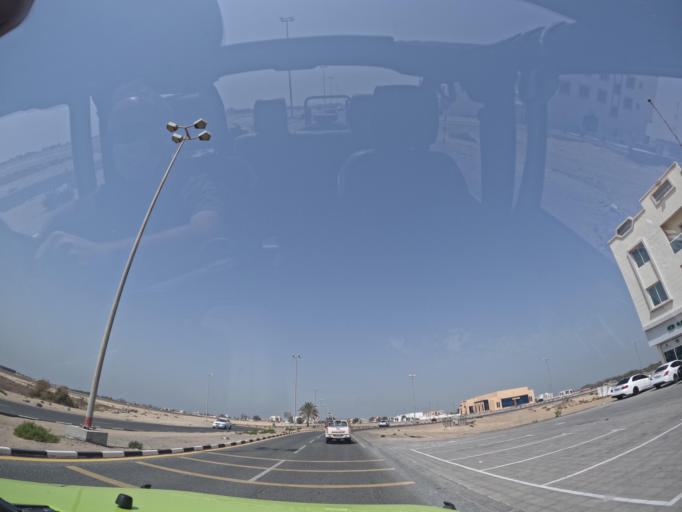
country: AE
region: Umm al Qaywayn
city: Umm al Qaywayn
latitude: 25.5207
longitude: 55.5542
